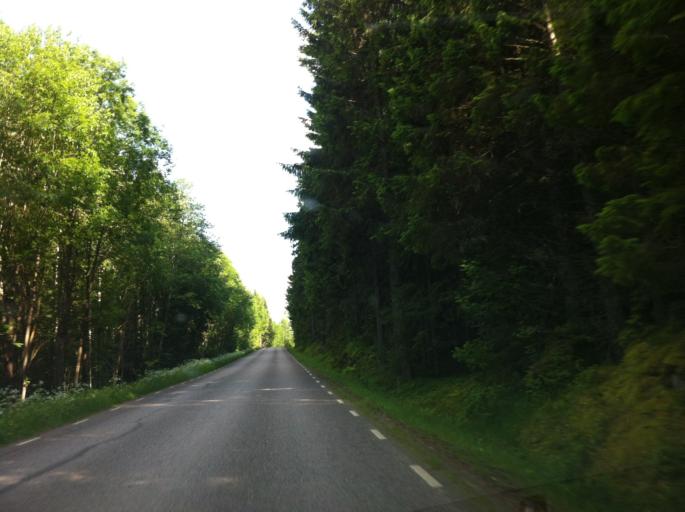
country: SE
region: Vaermland
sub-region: Kils Kommun
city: Kil
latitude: 59.6626
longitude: 13.3003
